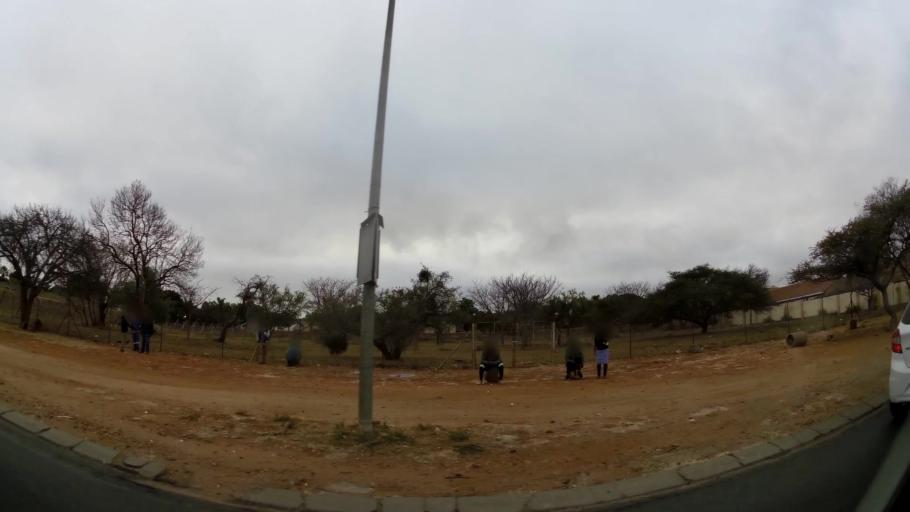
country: ZA
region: Limpopo
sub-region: Capricorn District Municipality
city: Polokwane
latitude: -23.8993
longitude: 29.4705
